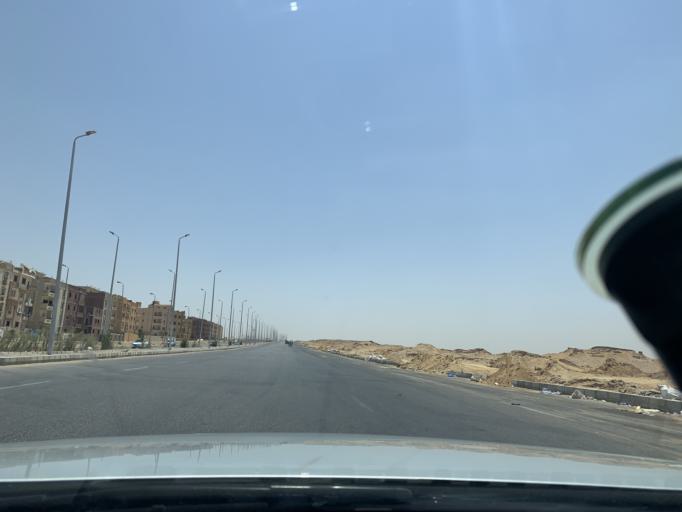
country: EG
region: Muhafazat al Qahirah
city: Cairo
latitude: 29.9979
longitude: 31.4686
